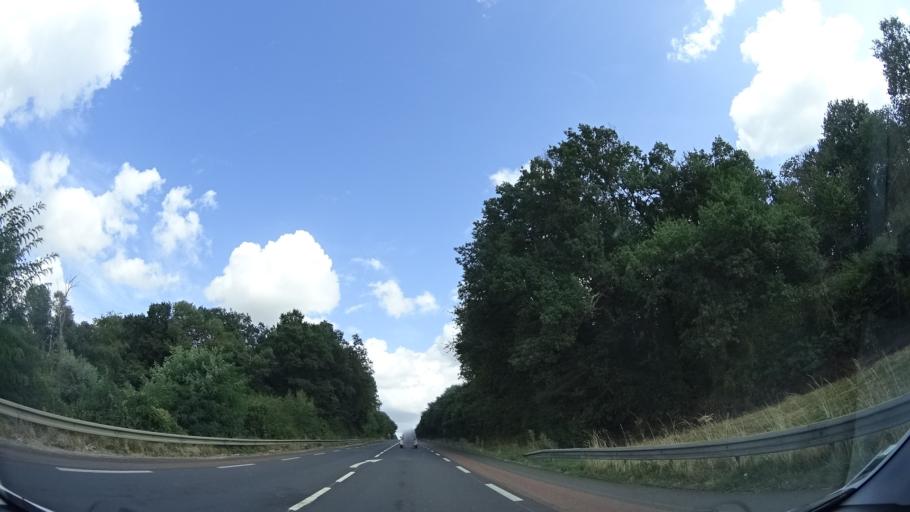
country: FR
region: Pays de la Loire
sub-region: Departement de la Sarthe
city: Coulans-sur-Gee
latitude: 48.0182
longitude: -0.0303
